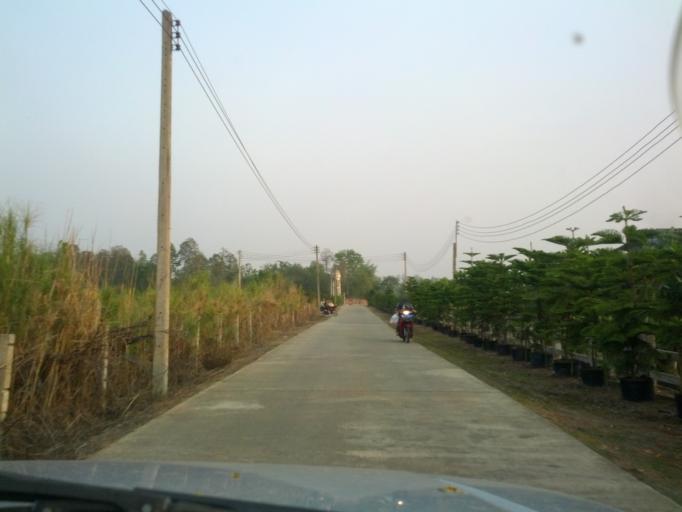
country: TH
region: Chiang Mai
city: San Sai
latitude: 18.9253
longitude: 99.0141
